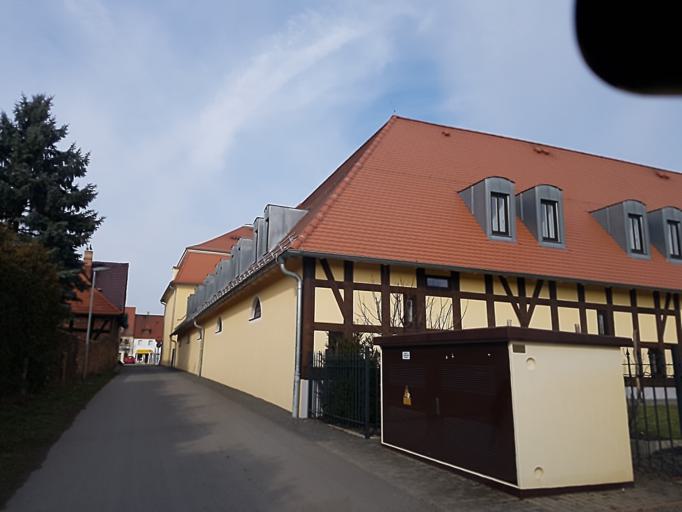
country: DE
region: Brandenburg
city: Doberlug-Kirchhain
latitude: 51.6102
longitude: 13.5503
